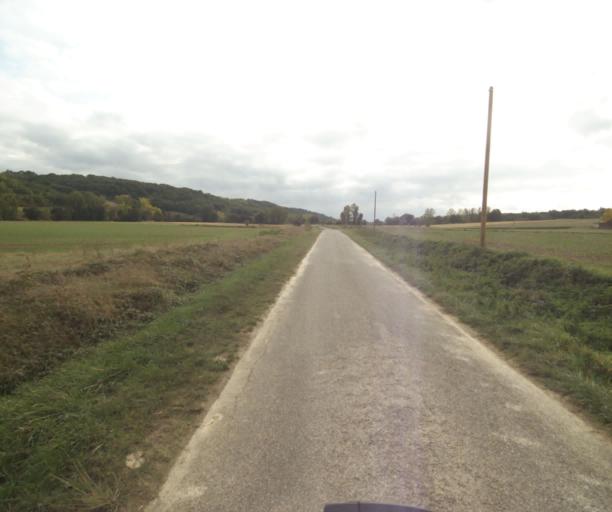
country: FR
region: Midi-Pyrenees
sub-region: Departement de la Haute-Garonne
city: Launac
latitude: 43.8420
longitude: 1.1104
